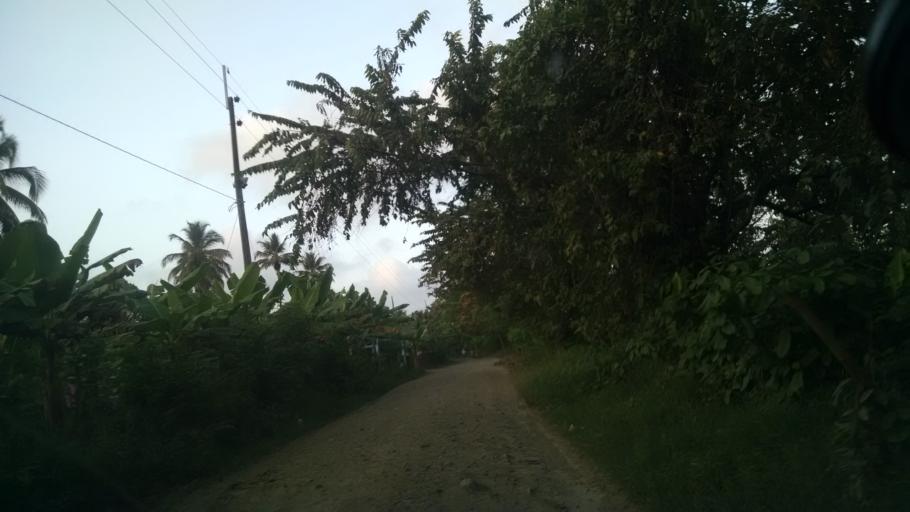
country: CO
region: Antioquia
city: San Juan de Uraba
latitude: 8.7293
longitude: -76.6052
